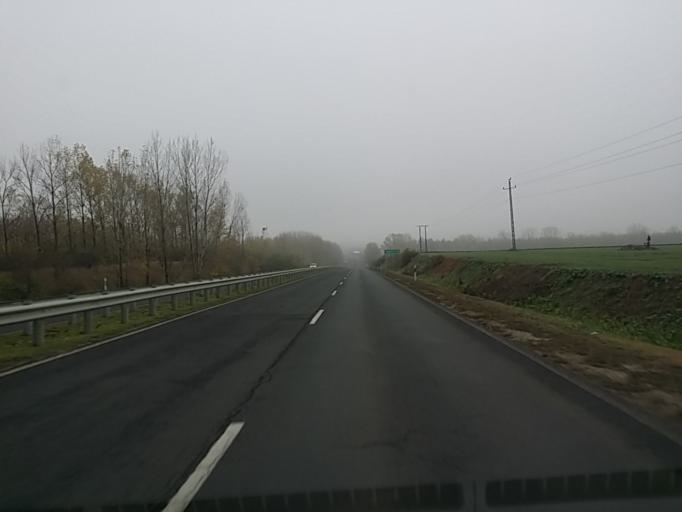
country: HU
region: Heves
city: Nagyrede
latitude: 47.7518
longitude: 19.8858
